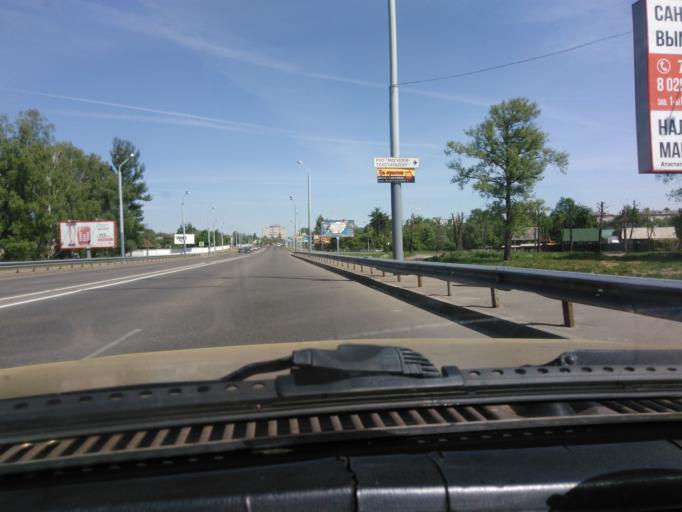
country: BY
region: Mogilev
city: Mahilyow
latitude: 53.9246
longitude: 30.3500
